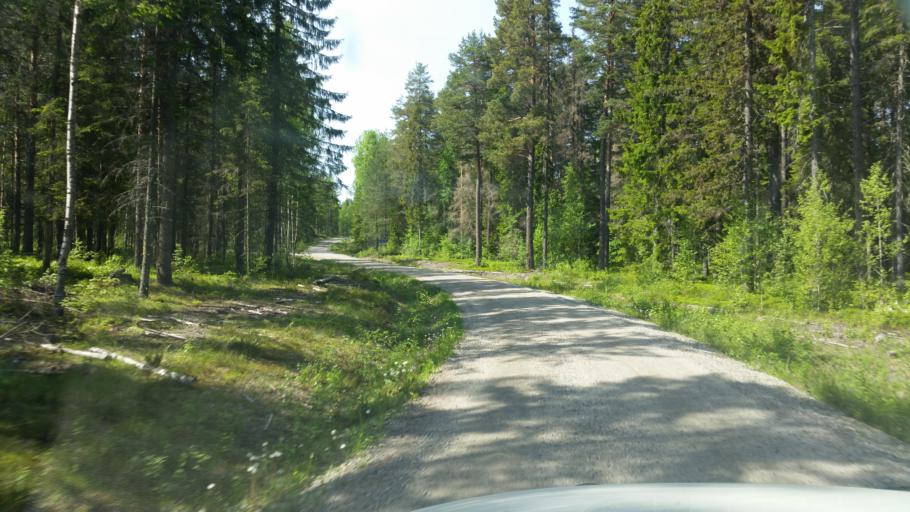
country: SE
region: Gaevleborg
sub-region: Hudiksvalls Kommun
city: Hudiksvall
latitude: 61.8200
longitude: 17.1028
